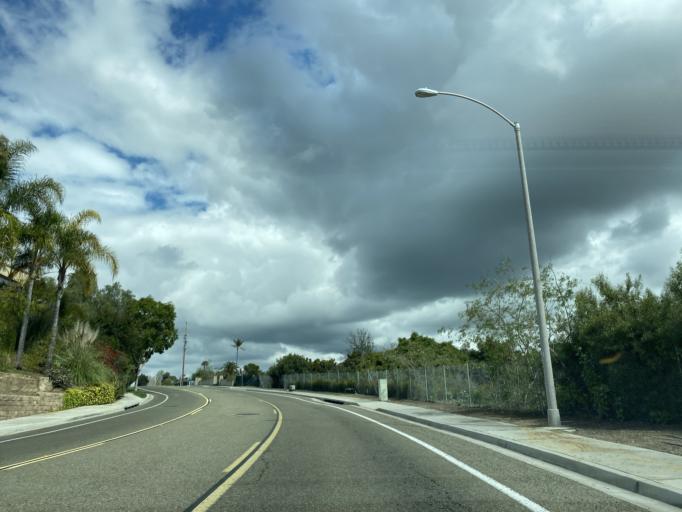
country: US
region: California
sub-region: San Diego County
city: Encinitas
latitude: 33.0491
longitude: -117.2793
